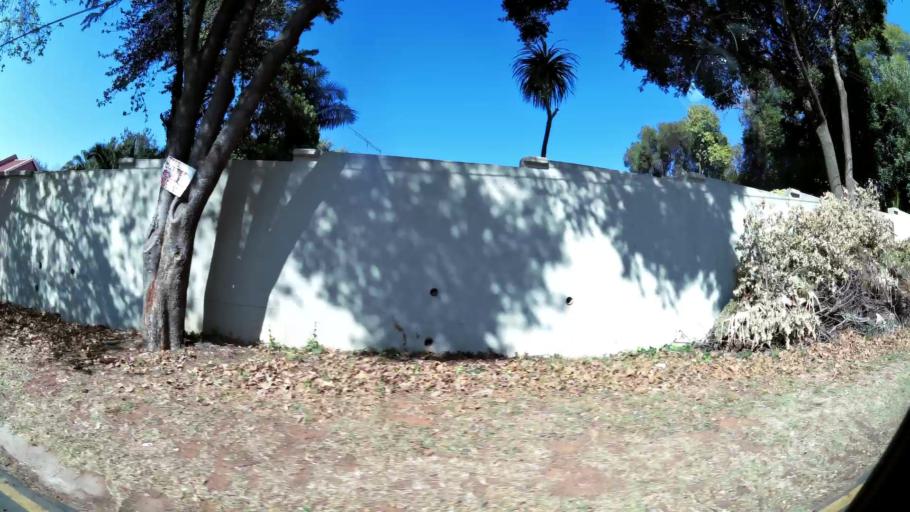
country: ZA
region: Gauteng
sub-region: City of Johannesburg Metropolitan Municipality
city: Roodepoort
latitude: -26.1392
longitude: 27.9075
